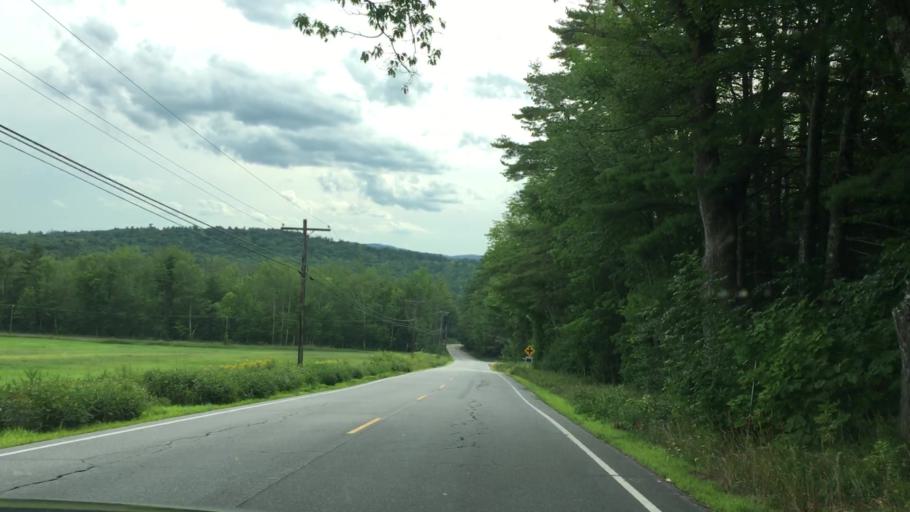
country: US
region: New Hampshire
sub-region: Carroll County
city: Center Harbor
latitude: 43.7067
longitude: -71.4912
